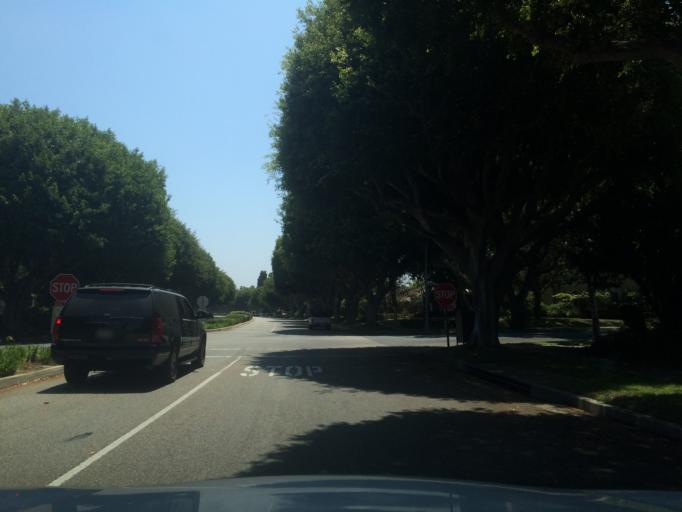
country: US
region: California
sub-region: Los Angeles County
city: Beverly Hills
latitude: 34.0757
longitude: -118.4113
